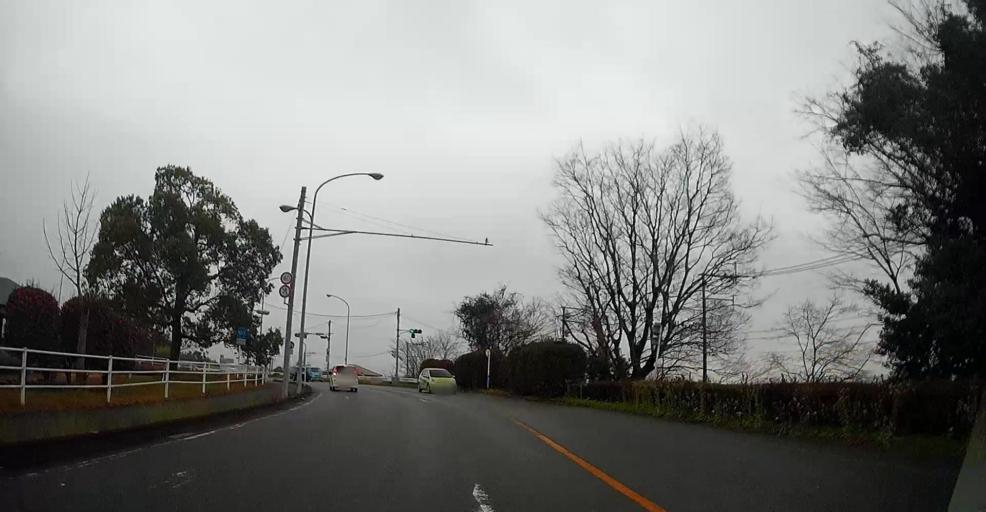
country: JP
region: Kumamoto
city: Kumamoto
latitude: 32.7614
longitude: 130.7528
